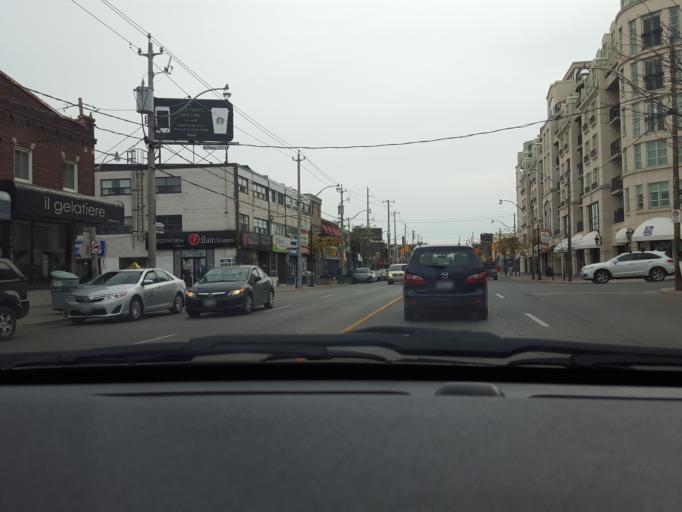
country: CA
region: Ontario
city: Toronto
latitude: 43.7054
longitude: -79.3890
